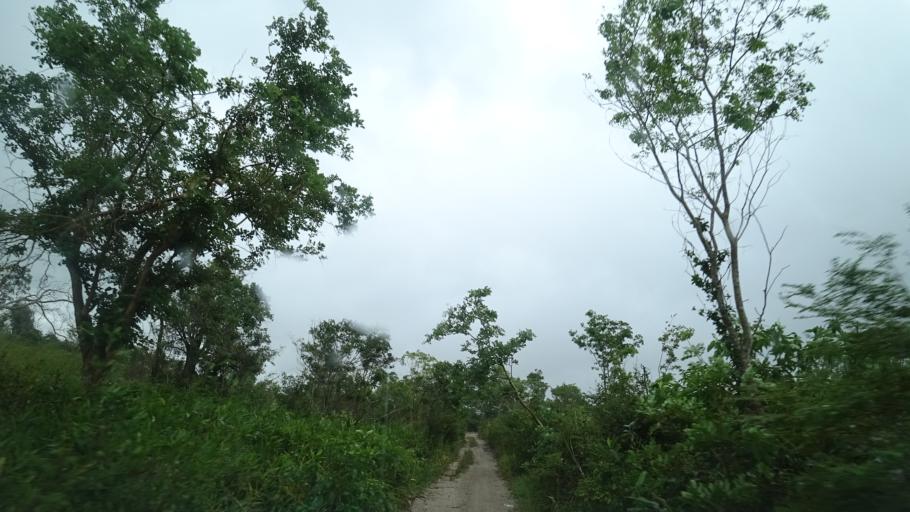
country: MZ
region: Sofala
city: Dondo
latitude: -19.5517
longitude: 35.0543
